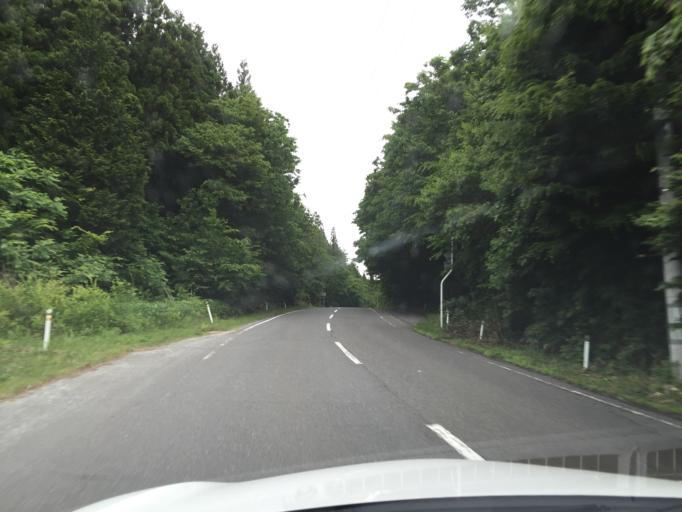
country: JP
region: Fukushima
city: Funehikimachi-funehiki
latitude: 37.3147
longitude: 140.7075
